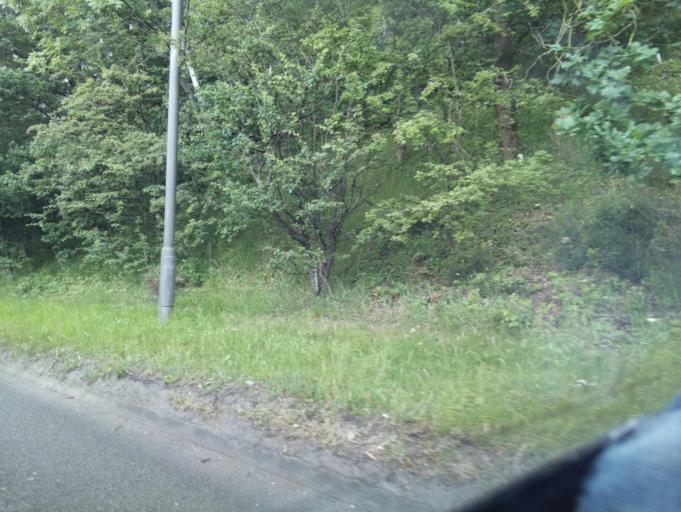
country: GB
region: England
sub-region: Dudley
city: Kingswinford
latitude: 52.5353
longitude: -2.1775
